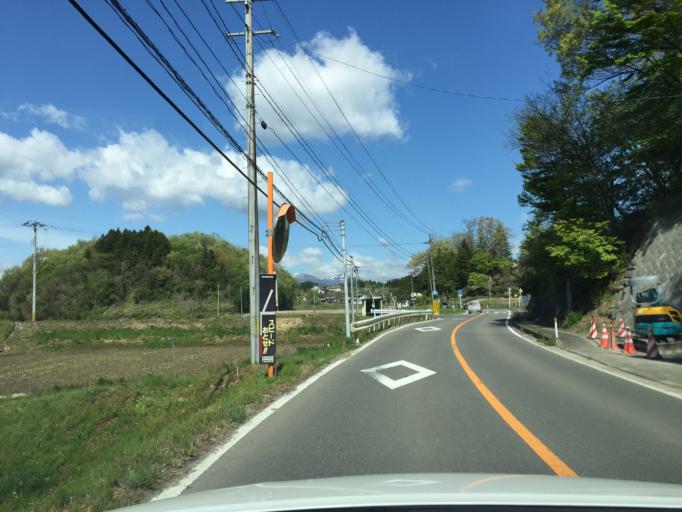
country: JP
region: Fukushima
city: Nihommatsu
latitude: 37.5705
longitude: 140.4759
